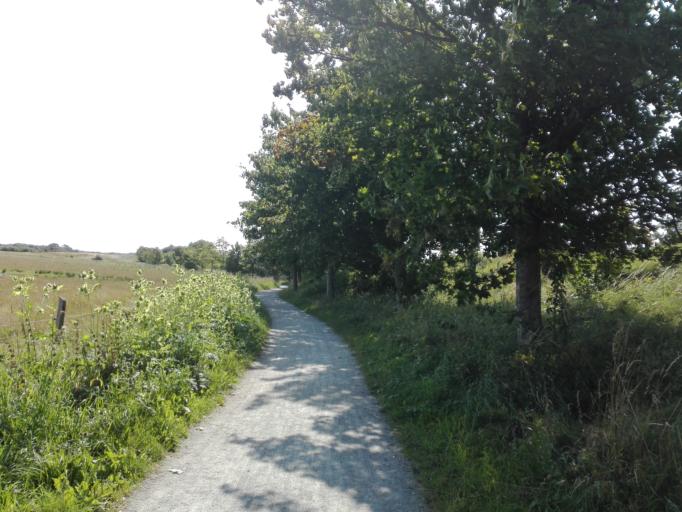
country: DK
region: Central Jutland
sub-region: Arhus Kommune
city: Lystrup
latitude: 56.2147
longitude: 10.2104
